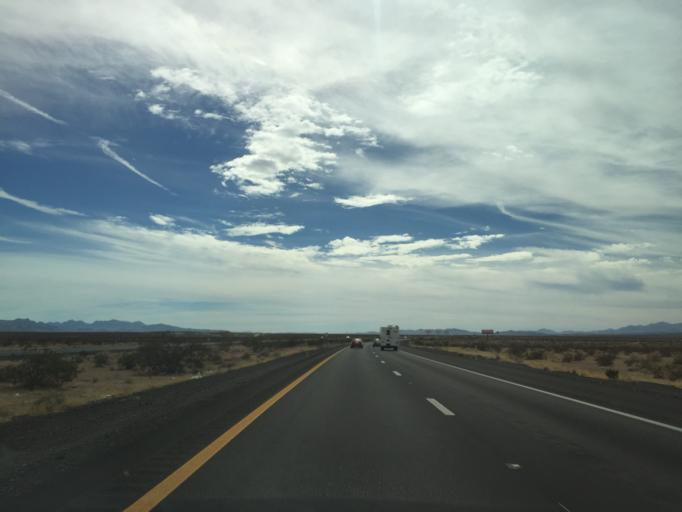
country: US
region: Nevada
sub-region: Clark County
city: Moapa Town
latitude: 36.5855
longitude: -114.6517
